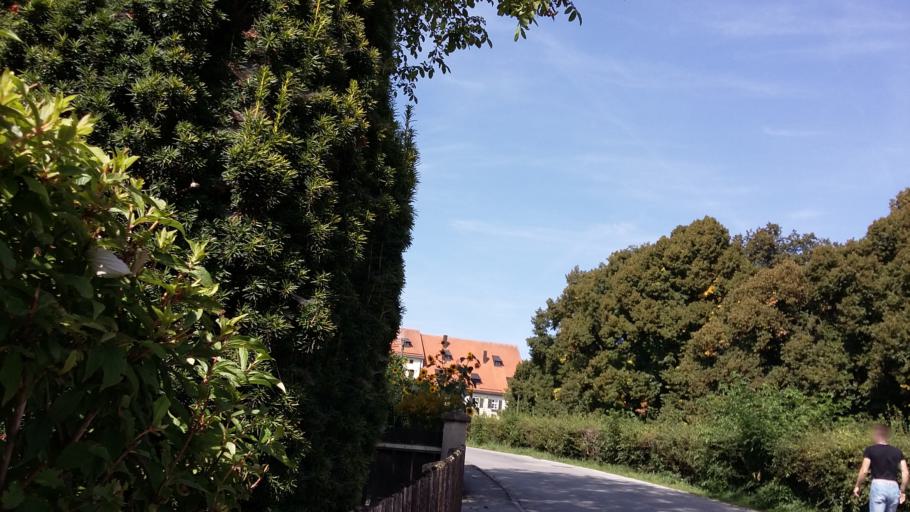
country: DE
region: Bavaria
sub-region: Upper Bavaria
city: Bernried
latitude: 47.8671
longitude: 11.2942
